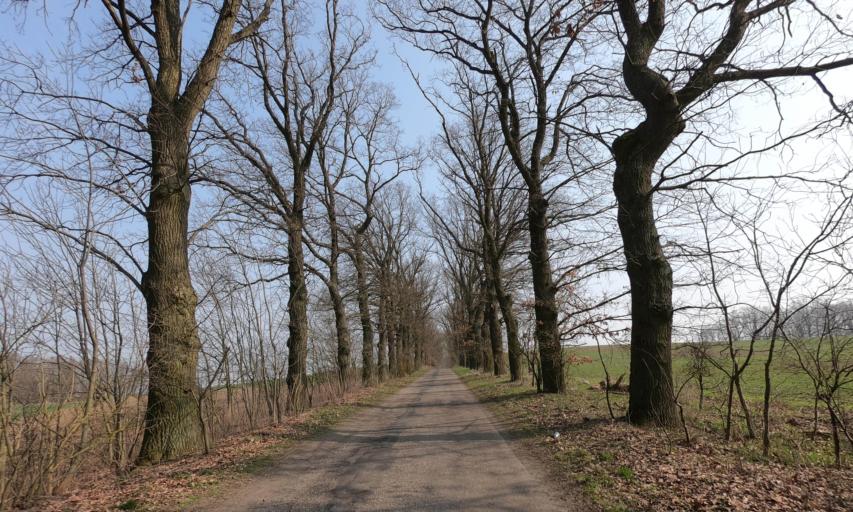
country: PL
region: West Pomeranian Voivodeship
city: Trzcinsko Zdroj
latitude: 52.9356
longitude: 14.6892
